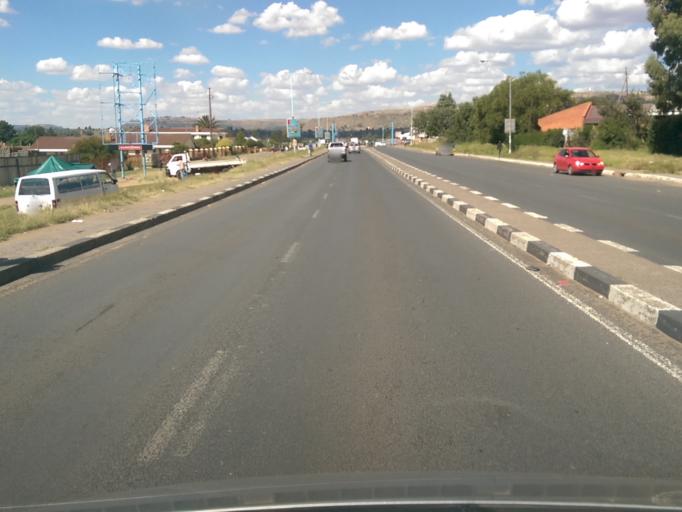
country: LS
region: Maseru
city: Maseru
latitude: -29.3142
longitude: 27.5041
